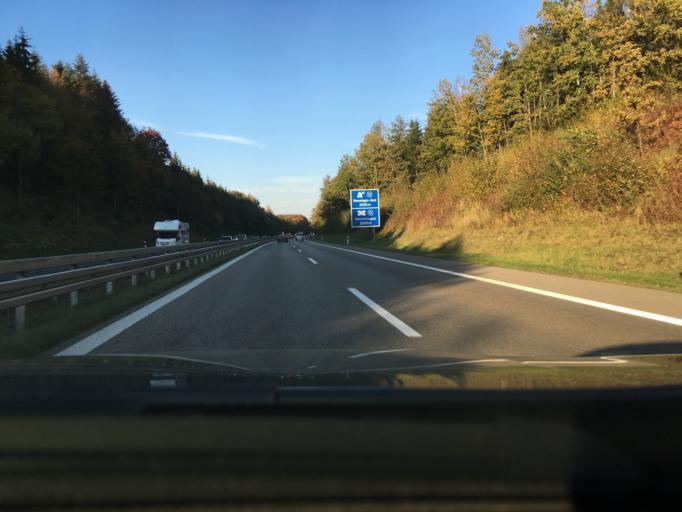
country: DE
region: Bavaria
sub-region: Swabia
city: Buxheim
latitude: 47.9785
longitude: 10.1234
